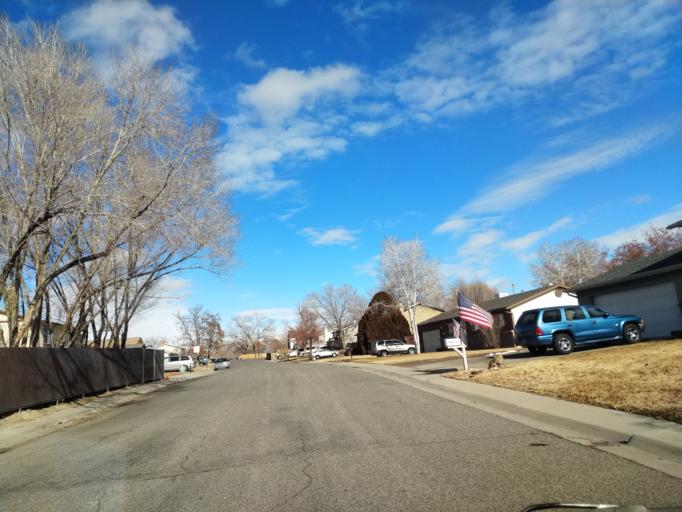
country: US
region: Colorado
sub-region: Mesa County
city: Fruitvale
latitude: 39.0757
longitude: -108.4878
